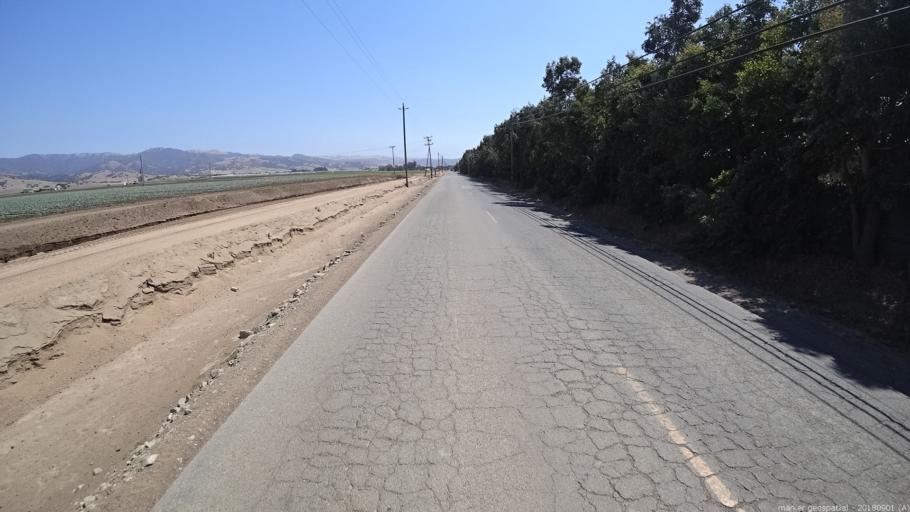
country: US
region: California
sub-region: Monterey County
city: Chualar
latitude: 36.6233
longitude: -121.5205
